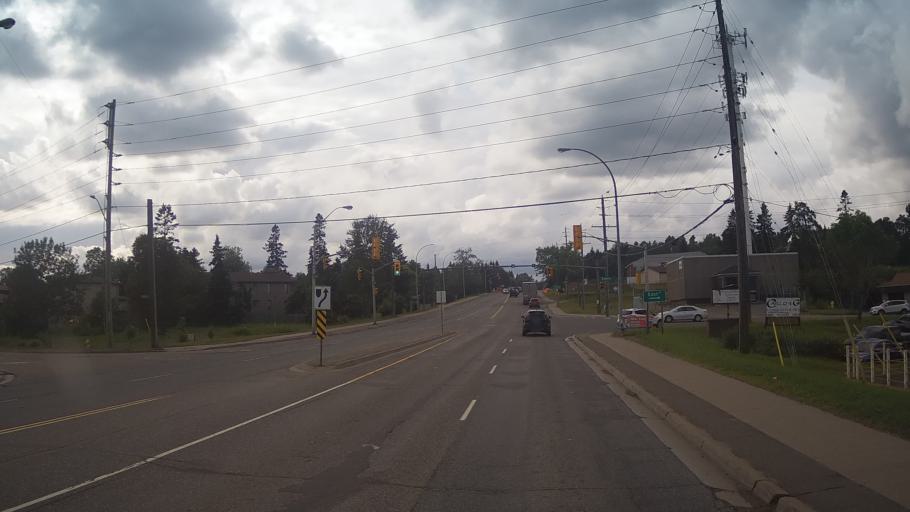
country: CA
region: Ontario
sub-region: Thunder Bay District
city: Thunder Bay
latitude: 48.4524
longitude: -89.2560
